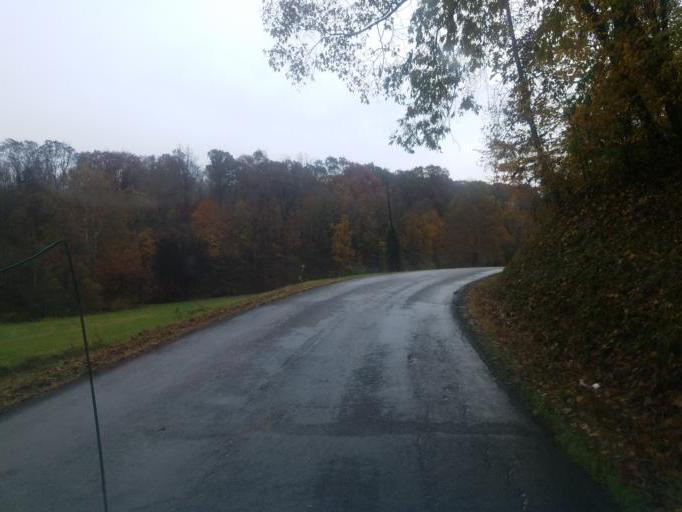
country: US
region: Ohio
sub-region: Washington County
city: Beverly
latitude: 39.5504
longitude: -81.6600
